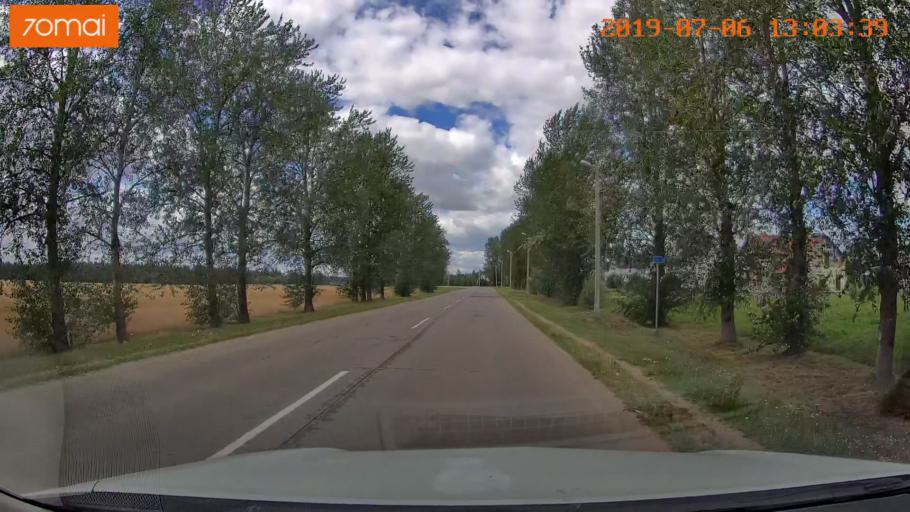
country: BY
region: Minsk
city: Dzyarzhynsk
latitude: 53.6899
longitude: 27.0984
